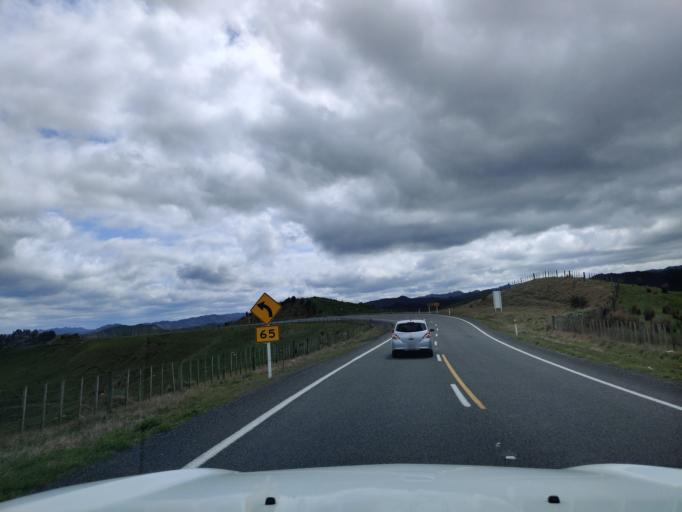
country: NZ
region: Manawatu-Wanganui
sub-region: Wanganui District
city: Wanganui
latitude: -39.7851
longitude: 175.2302
